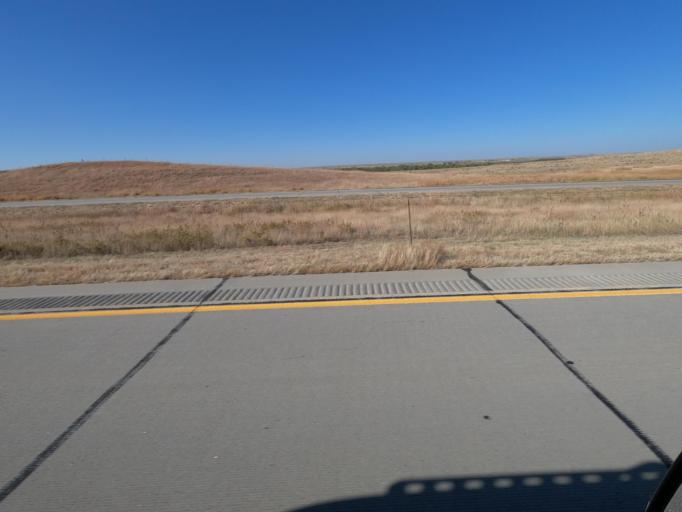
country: US
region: Colorado
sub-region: Sedgwick County
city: Julesburg
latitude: 40.9311
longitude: -102.3236
